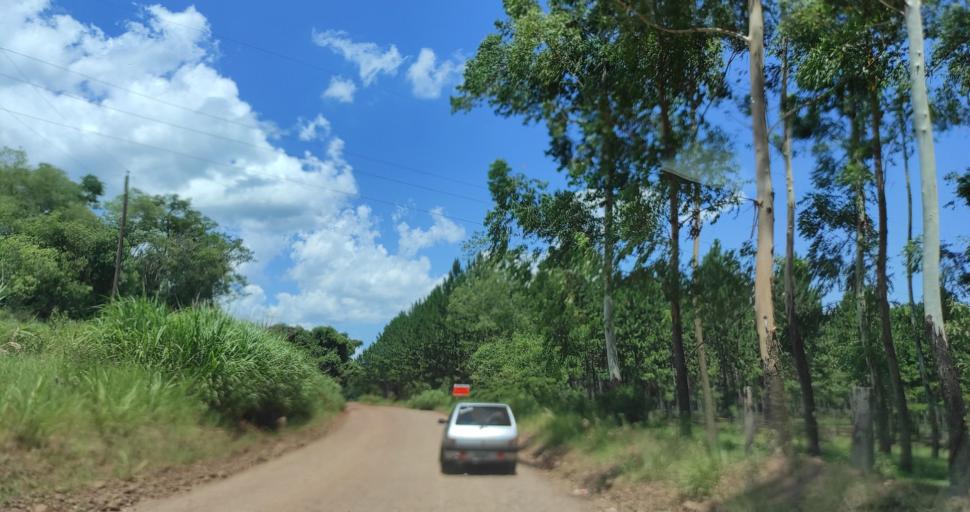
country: AR
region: Misiones
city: Ruiz de Montoya
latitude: -27.0417
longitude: -55.0106
